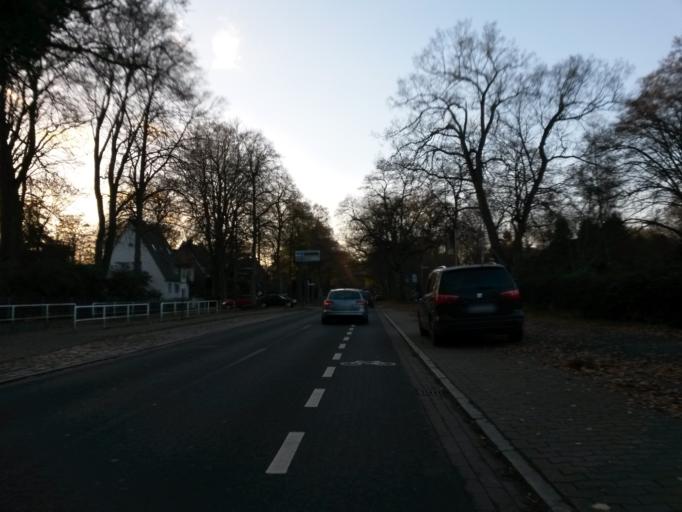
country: DE
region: Lower Saxony
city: Lilienthal
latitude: 53.0906
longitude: 8.8808
